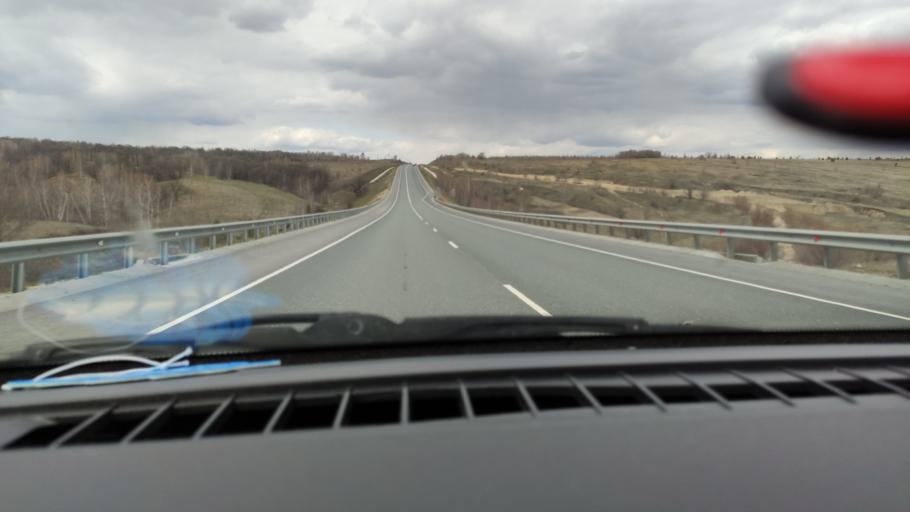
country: RU
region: Saratov
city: Shikhany
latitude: 52.1417
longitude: 47.2061
